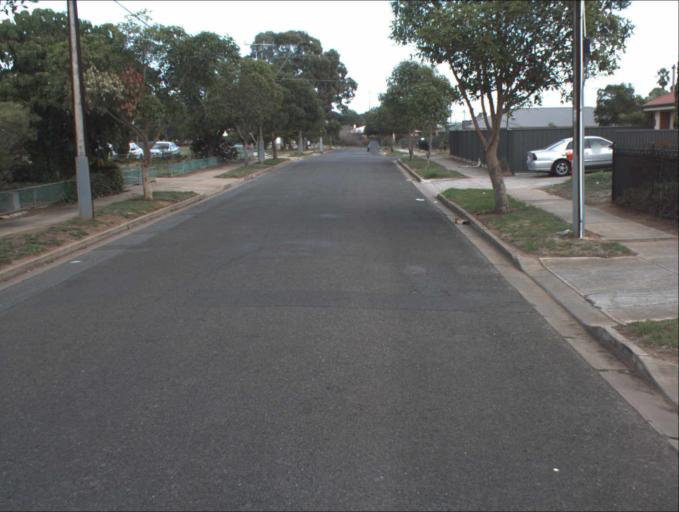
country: AU
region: South Australia
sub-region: Port Adelaide Enfield
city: Enfield
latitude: -34.8507
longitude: 138.5975
